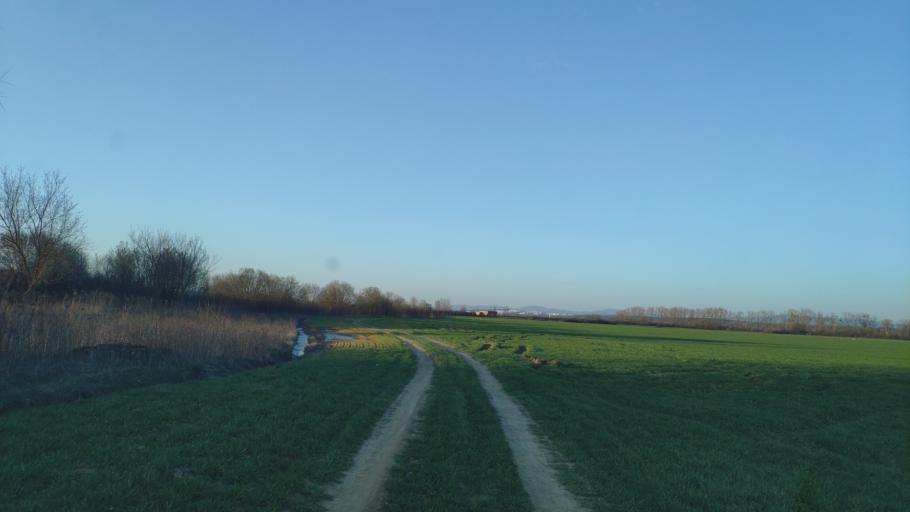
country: SK
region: Kosicky
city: Kosice
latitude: 48.6483
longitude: 21.2413
